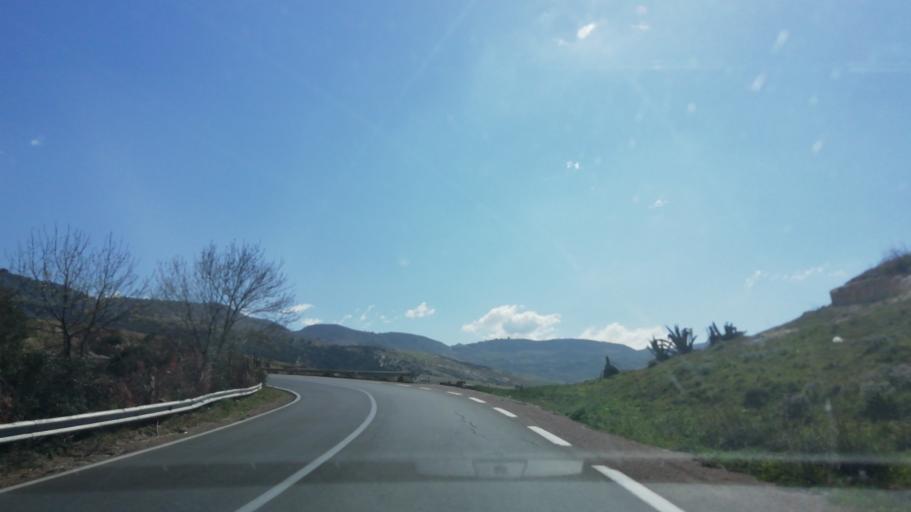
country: DZ
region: Mascara
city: Mascara
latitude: 35.4902
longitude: 0.1372
